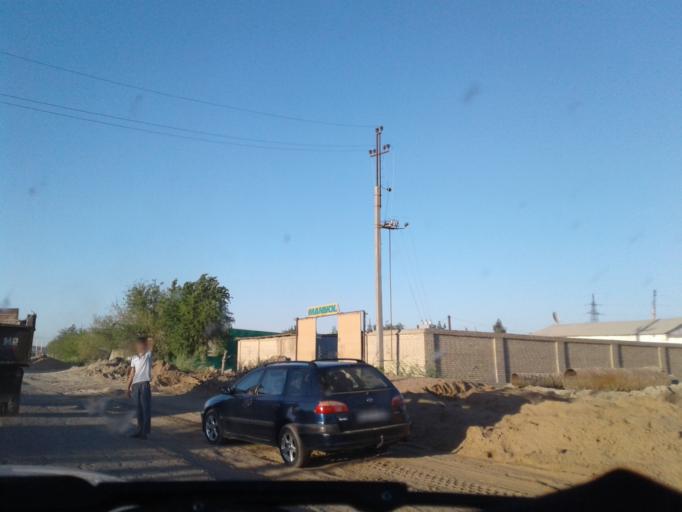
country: TM
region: Mary
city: Mary
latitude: 37.5683
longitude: 61.8291
